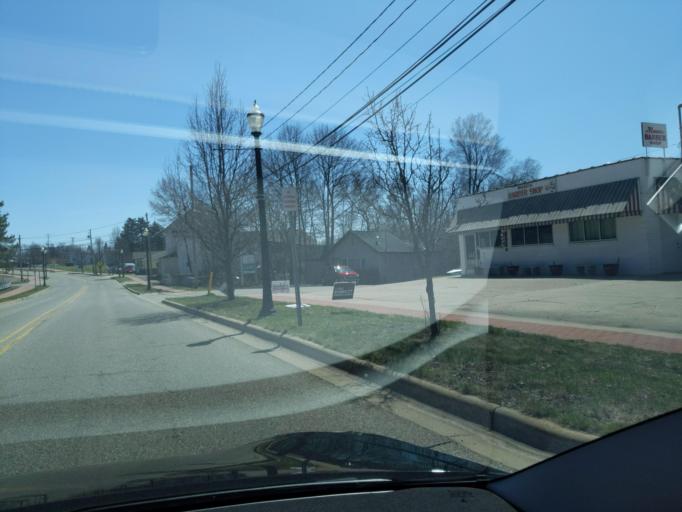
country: US
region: Michigan
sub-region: Ingham County
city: Mason
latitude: 42.5820
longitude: -84.4469
